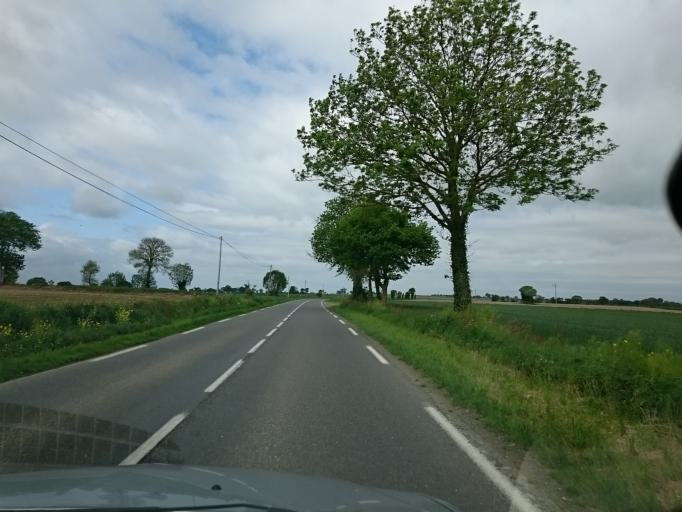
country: FR
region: Lower Normandy
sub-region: Departement de la Manche
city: Saint-James
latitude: 48.5500
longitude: -1.4012
